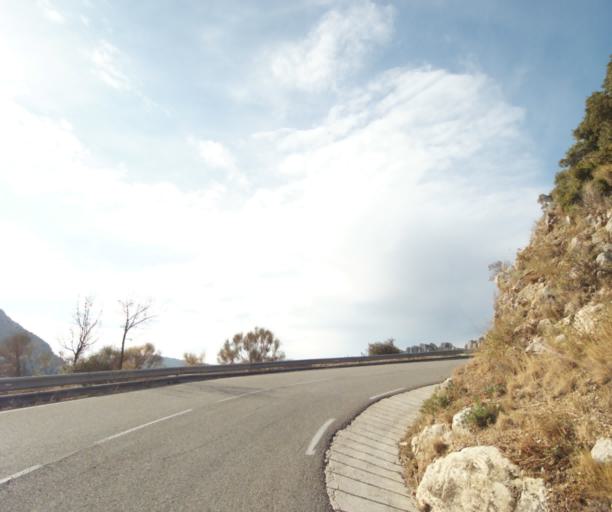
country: FR
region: Provence-Alpes-Cote d'Azur
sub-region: Departement des Bouches-du-Rhone
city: Gemenos
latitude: 43.3041
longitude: 5.6673
